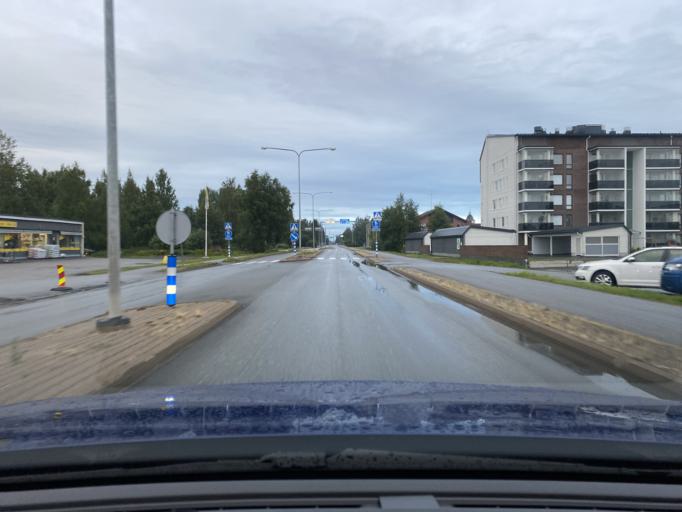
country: FI
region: Ostrobothnia
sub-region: Kyroenmaa
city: Laihia
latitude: 62.9813
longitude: 22.0066
